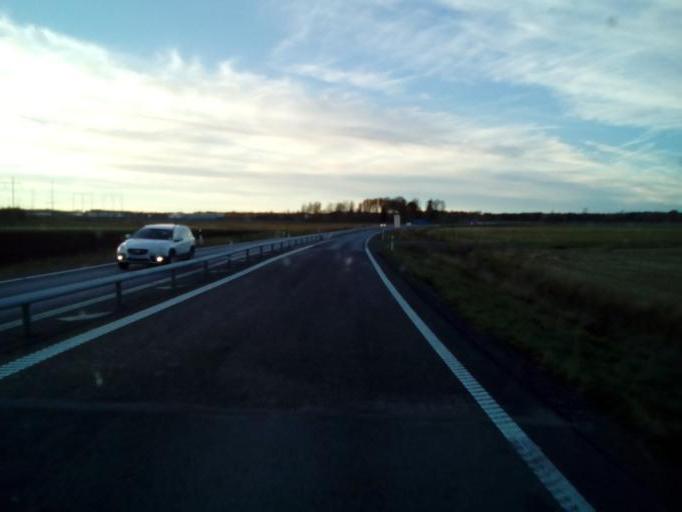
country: SE
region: OErebro
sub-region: Orebro Kommun
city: Orebro
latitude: 59.2085
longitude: 15.1976
